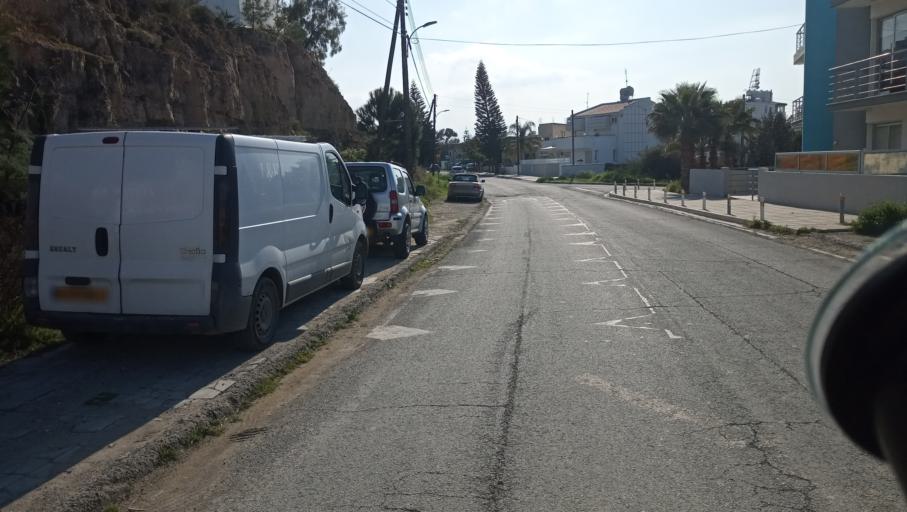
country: CY
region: Lefkosia
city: Nicosia
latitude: 35.1464
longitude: 33.3178
